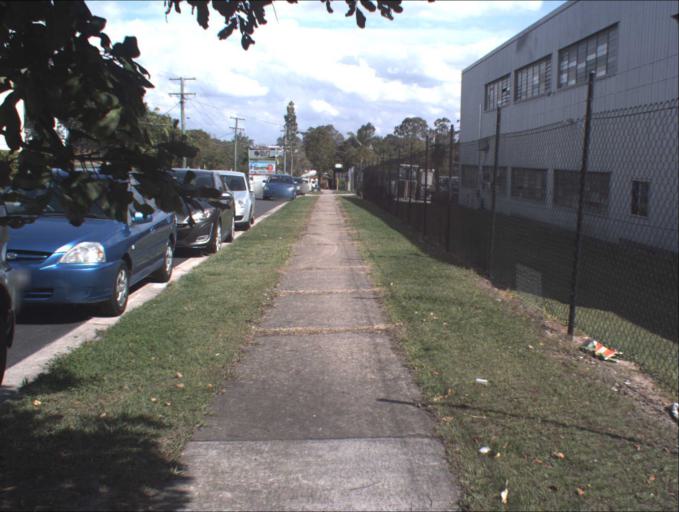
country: AU
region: Queensland
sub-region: Brisbane
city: Sunnybank Hills
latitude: -27.6600
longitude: 153.0328
